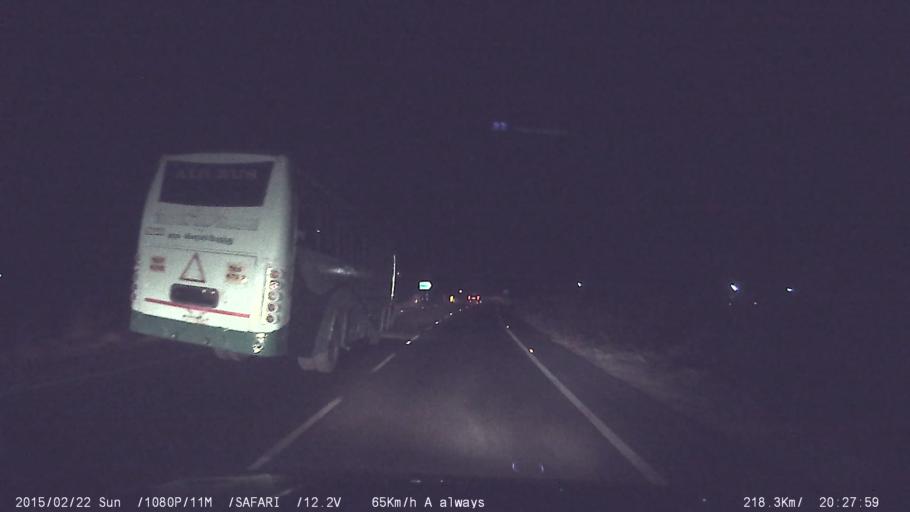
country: IN
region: Tamil Nadu
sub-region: Dindigul
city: Dindigul
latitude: 10.3259
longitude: 77.9169
